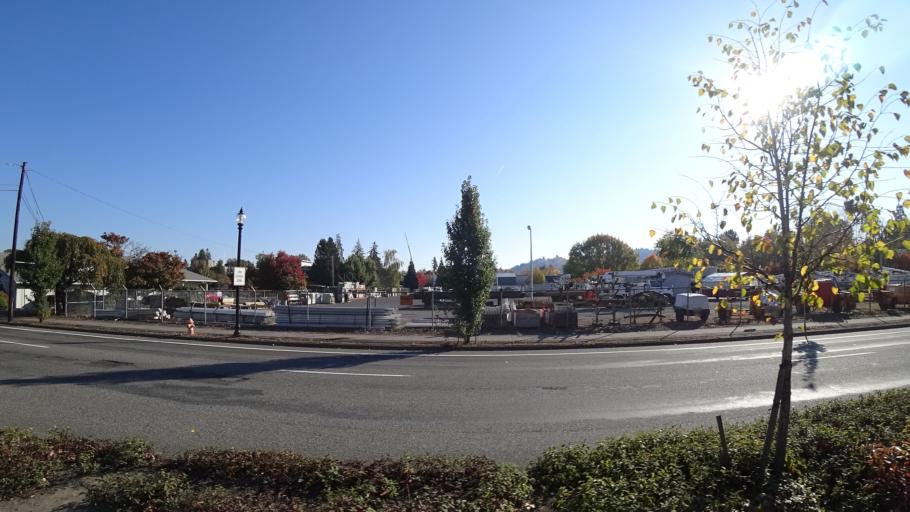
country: US
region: Oregon
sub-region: Multnomah County
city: Gresham
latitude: 45.5049
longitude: -122.4270
